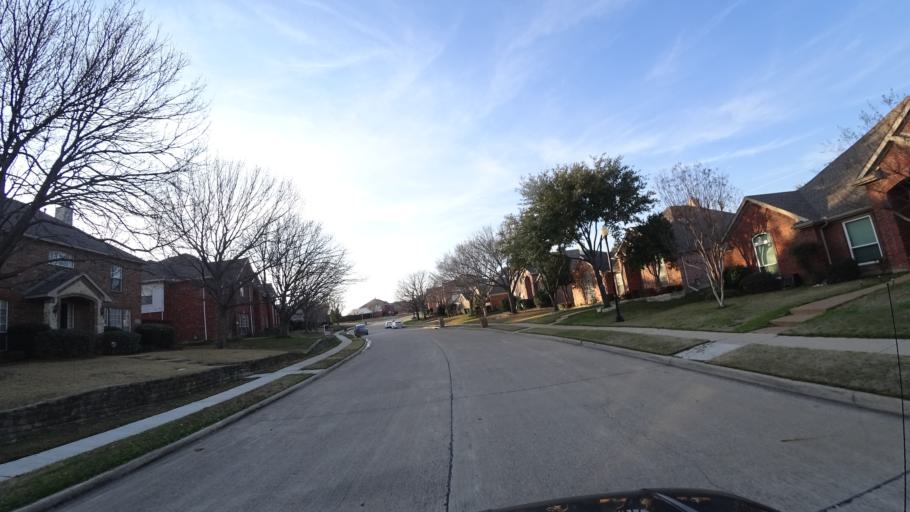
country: US
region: Texas
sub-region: Dallas County
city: Coppell
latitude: 32.9936
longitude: -96.9839
